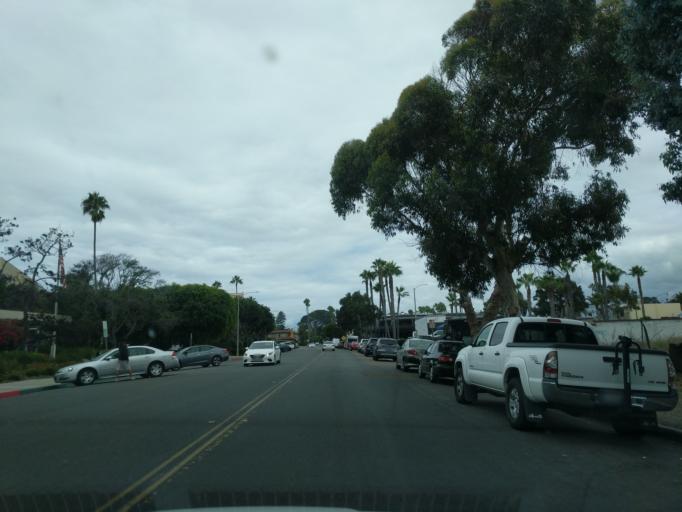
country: US
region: California
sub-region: San Diego County
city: Solana Beach
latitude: 32.9898
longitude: -117.2726
